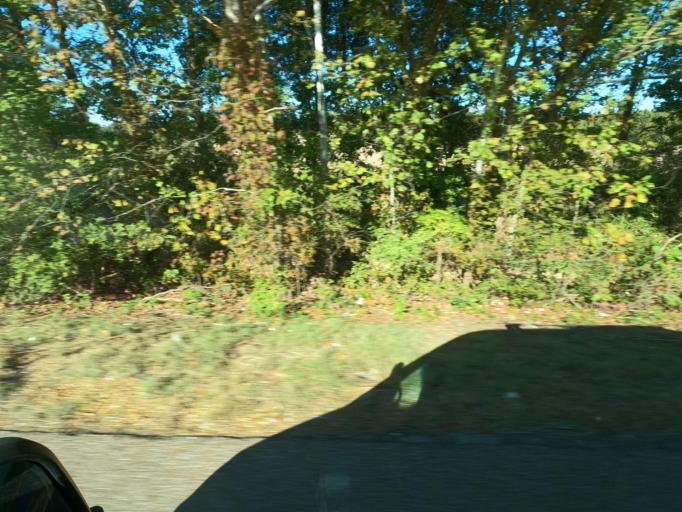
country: US
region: Tennessee
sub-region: Tipton County
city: Brighton
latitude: 35.5093
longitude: -89.7115
